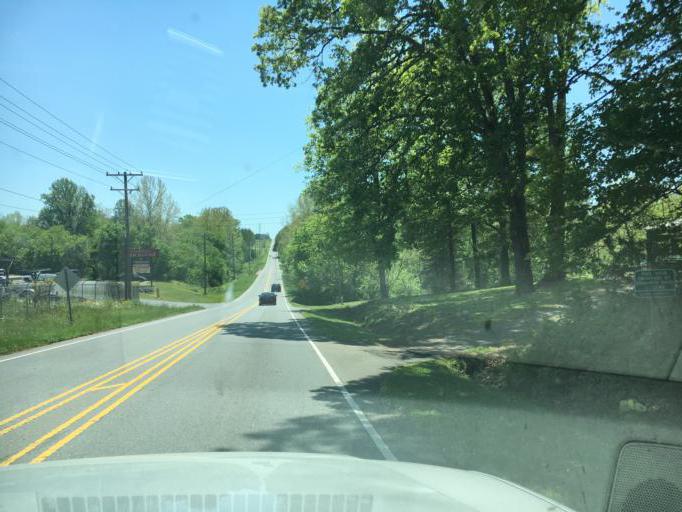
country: US
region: North Carolina
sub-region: Cleveland County
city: Shelby
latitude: 35.2437
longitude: -81.5667
